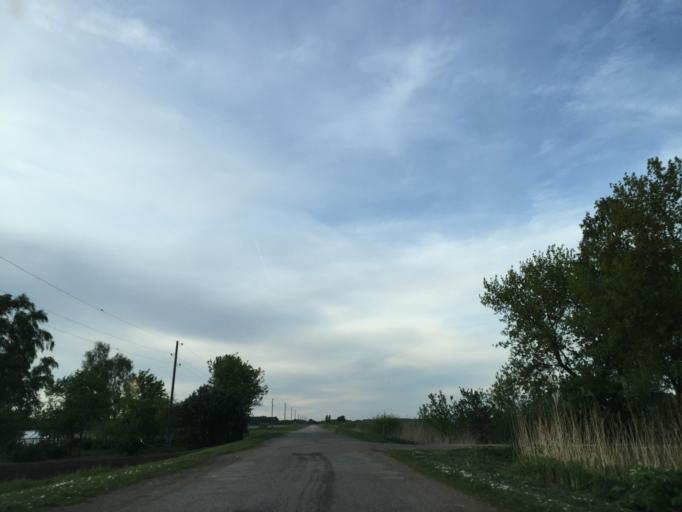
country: LV
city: Tireli
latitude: 56.7869
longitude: 23.5617
